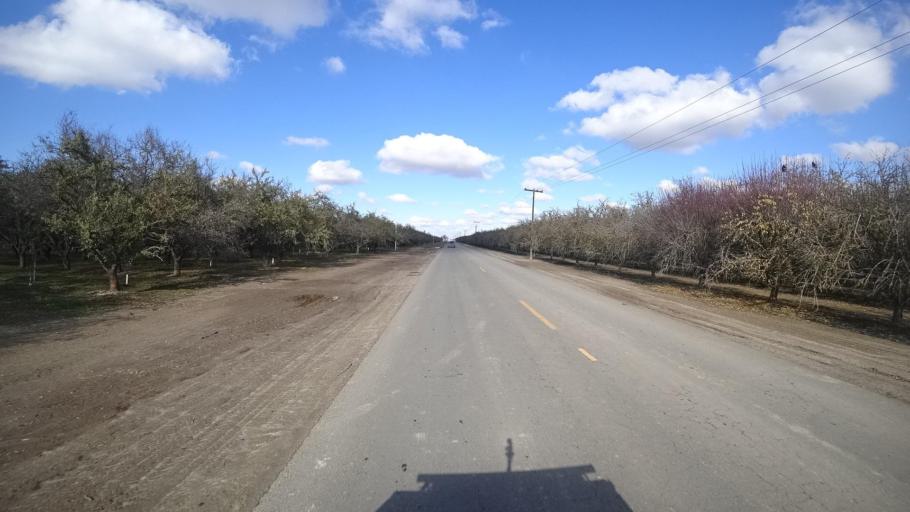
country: US
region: California
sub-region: Kern County
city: Delano
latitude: 35.7266
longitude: -119.3659
